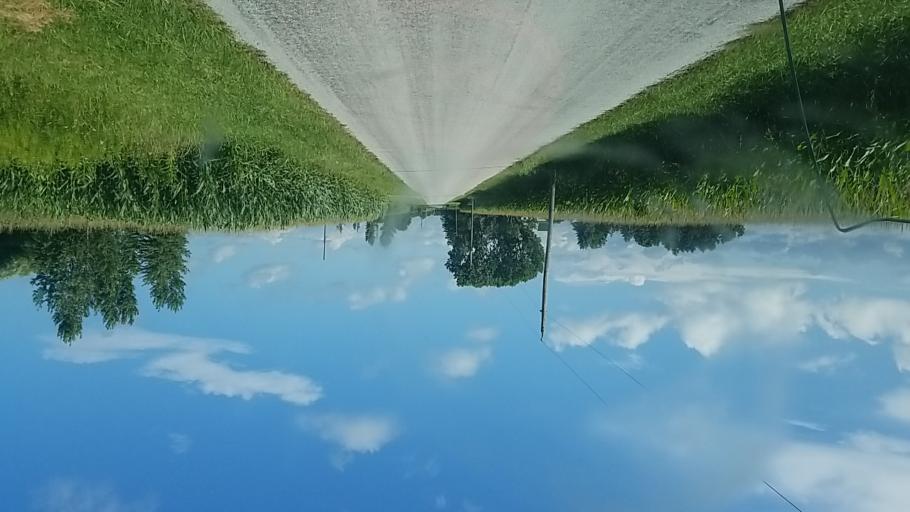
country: US
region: Ohio
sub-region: Hardin County
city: Kenton
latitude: 40.6930
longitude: -83.5309
